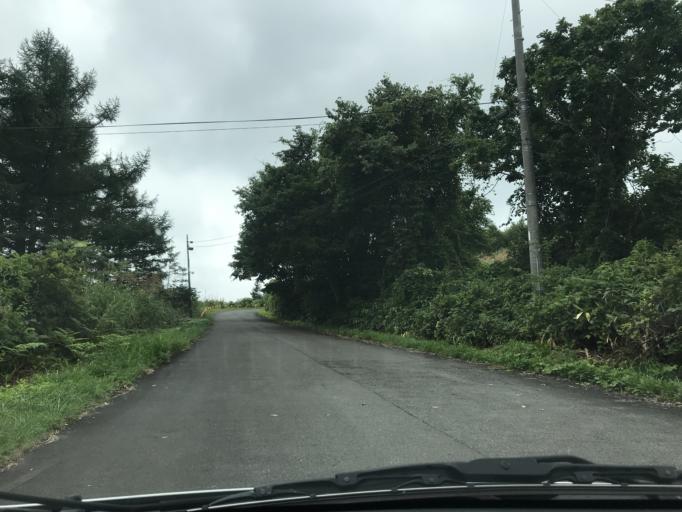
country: JP
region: Iwate
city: Ichinoseki
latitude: 38.9357
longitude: 140.8391
